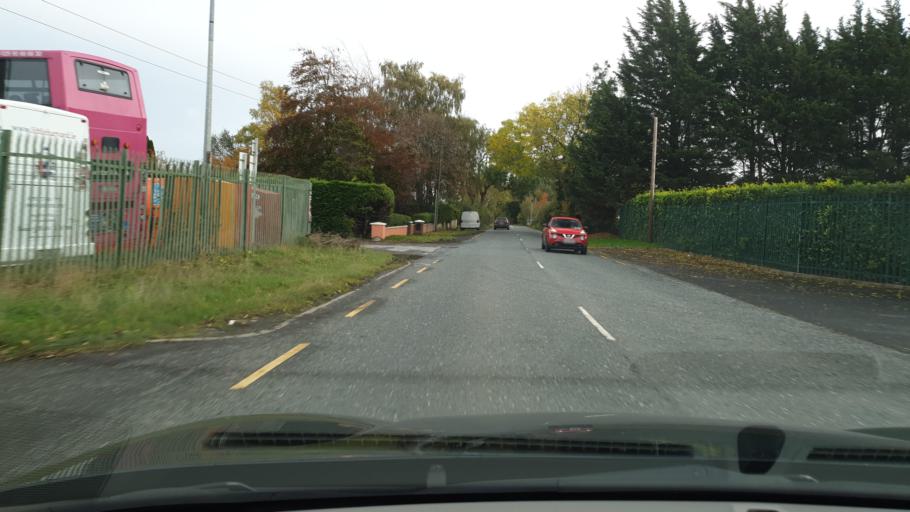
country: IE
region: Leinster
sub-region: An Mhi
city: Ashbourne
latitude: 53.5003
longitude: -6.4291
